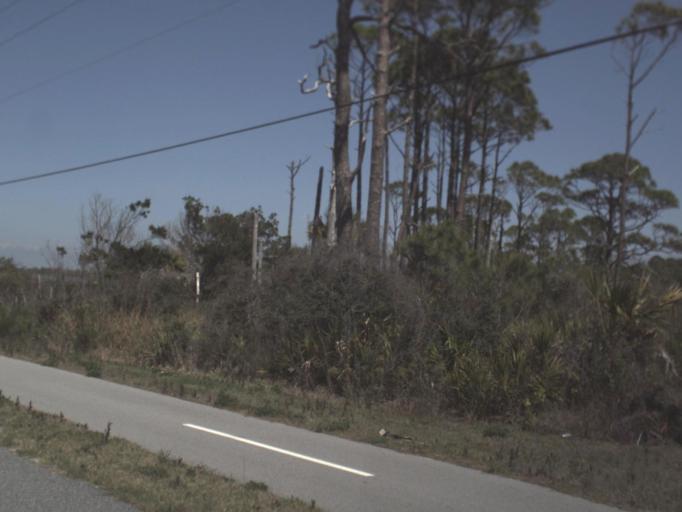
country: US
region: Florida
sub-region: Gulf County
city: Port Saint Joe
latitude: 29.6848
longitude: -85.3679
